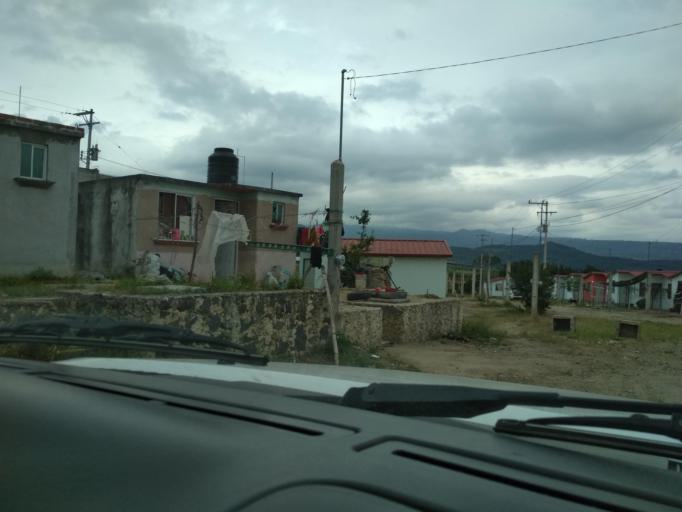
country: MX
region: Veracruz
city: El Castillo
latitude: 19.5847
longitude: -96.8299
